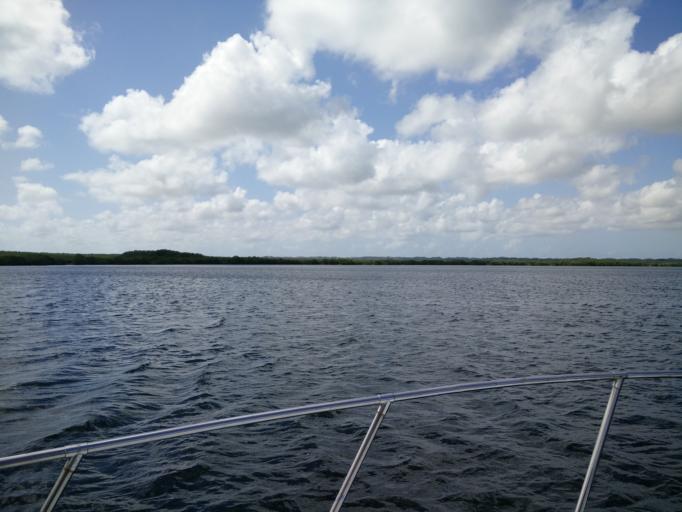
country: GP
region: Guadeloupe
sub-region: Guadeloupe
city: Petit-Canal
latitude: 16.3731
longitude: -61.4997
